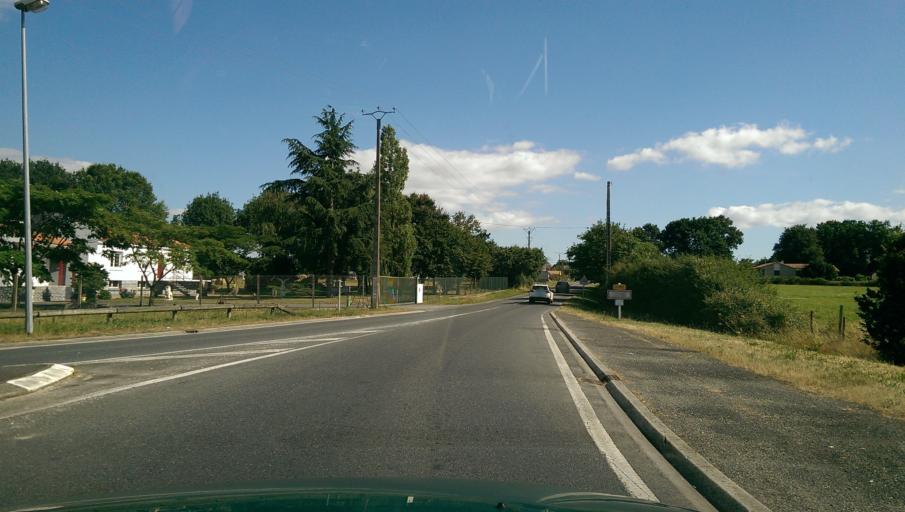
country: FR
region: Pays de la Loire
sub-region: Departement de la Loire-Atlantique
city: Lege
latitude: 46.8912
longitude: -1.6013
